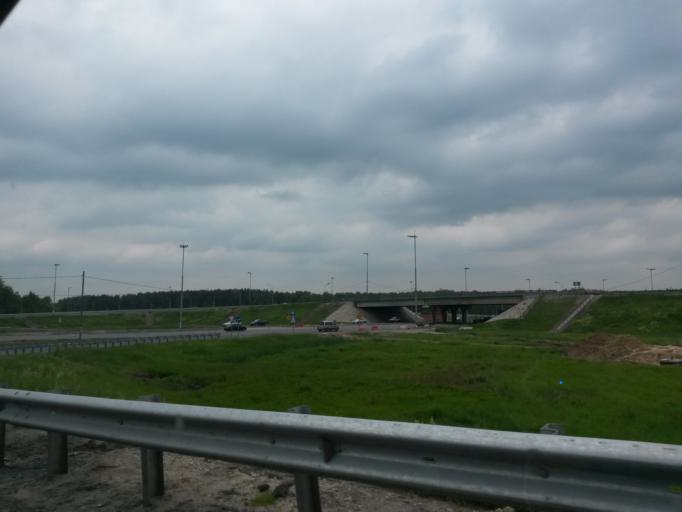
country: RU
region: Moskovskaya
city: Lyubuchany
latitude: 55.1855
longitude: 37.5365
